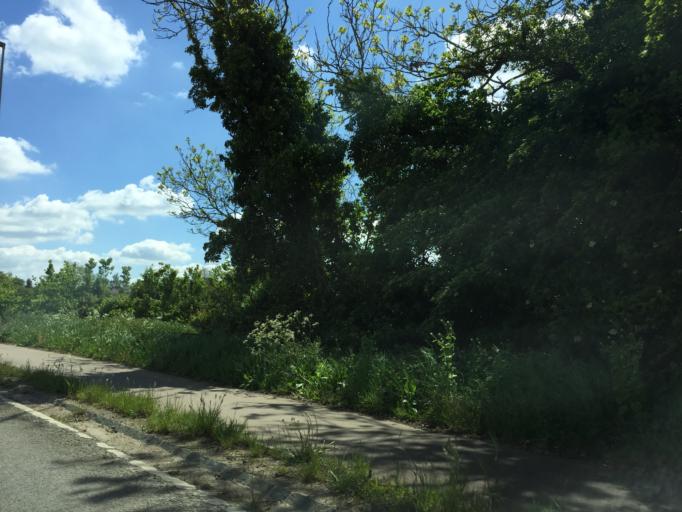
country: GB
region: England
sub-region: Milton Keynes
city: Wavendon
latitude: 52.0289
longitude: -0.6725
